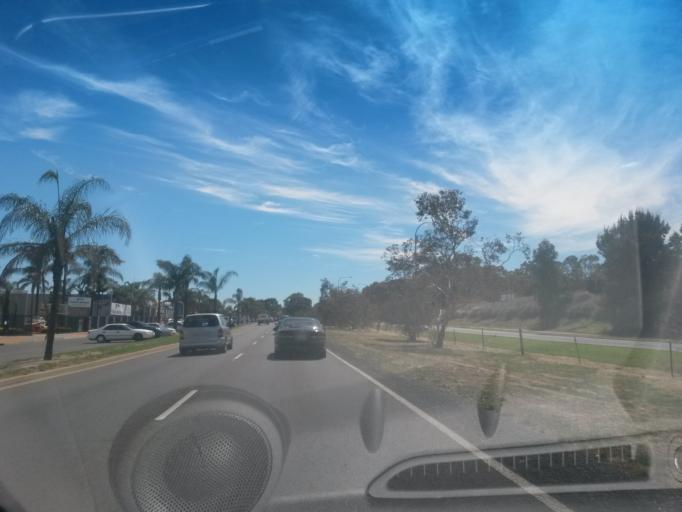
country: AU
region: South Australia
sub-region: Salisbury
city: Salisbury
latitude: -34.7708
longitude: 138.6653
